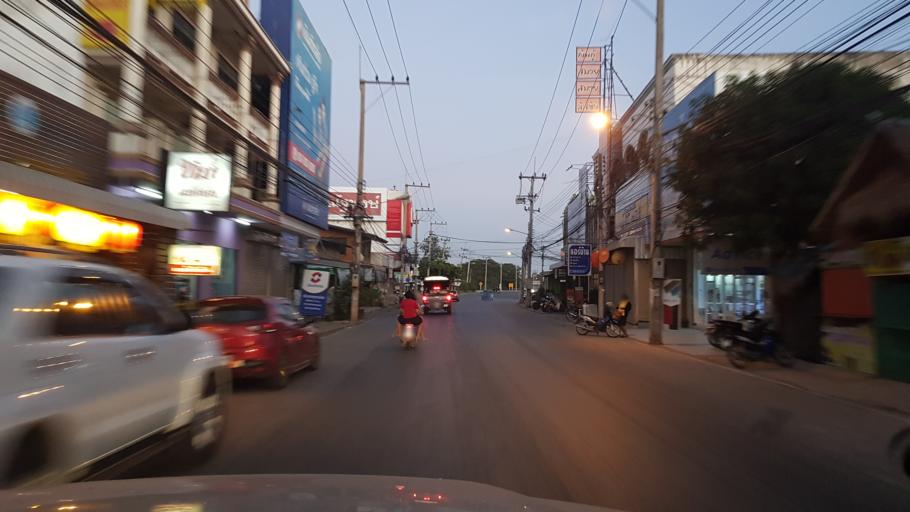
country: TH
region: Chaiyaphum
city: Phu Khiao
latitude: 16.3656
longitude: 102.1377
